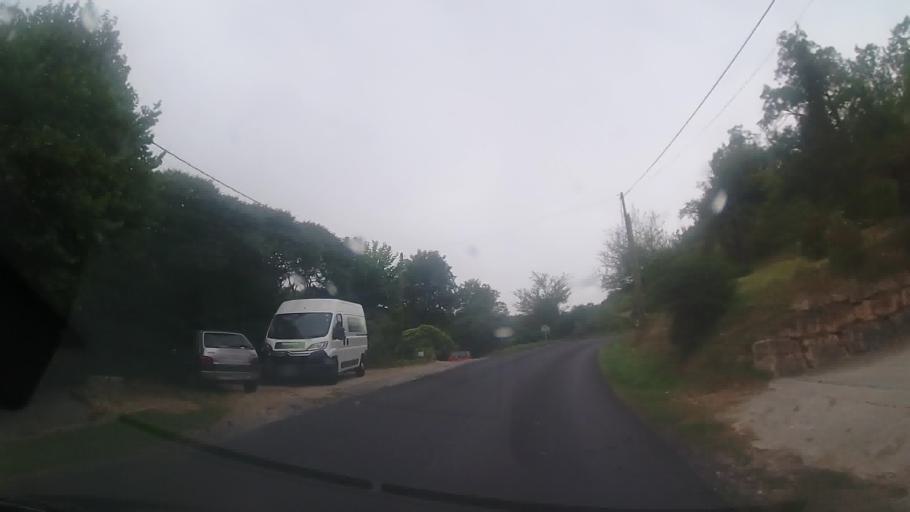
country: FR
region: Aquitaine
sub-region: Departement de la Dordogne
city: Cenac-et-Saint-Julien
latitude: 44.7989
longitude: 1.1966
